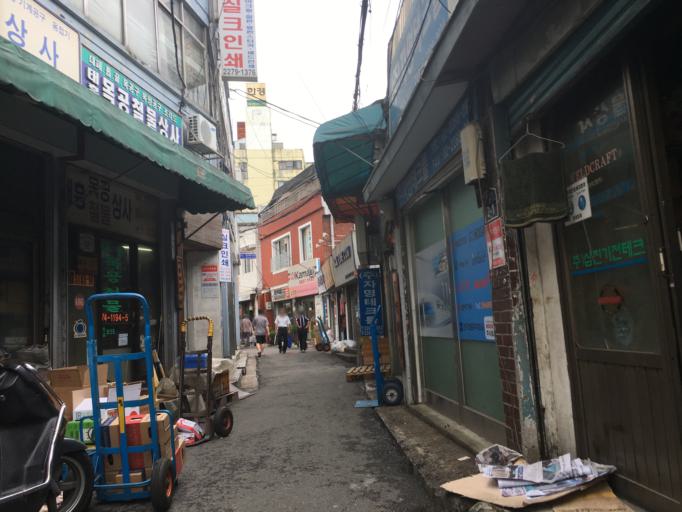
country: KR
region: Seoul
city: Seoul
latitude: 37.5675
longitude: 126.9922
